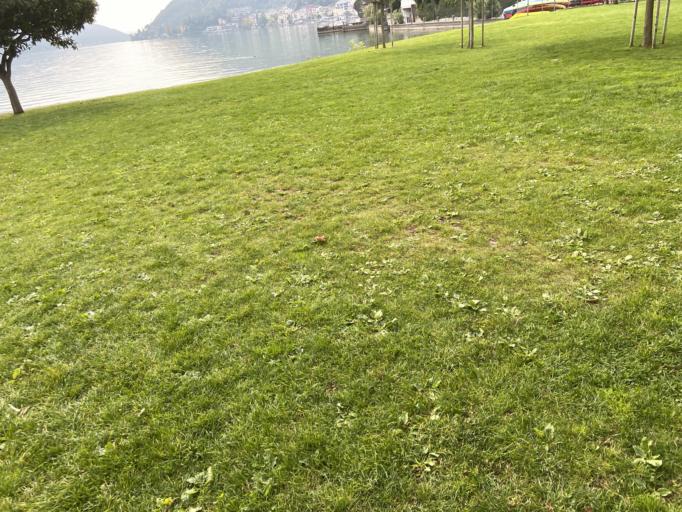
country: CH
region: Ticino
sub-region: Lugano District
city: Melide
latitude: 45.9530
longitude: 8.9489
